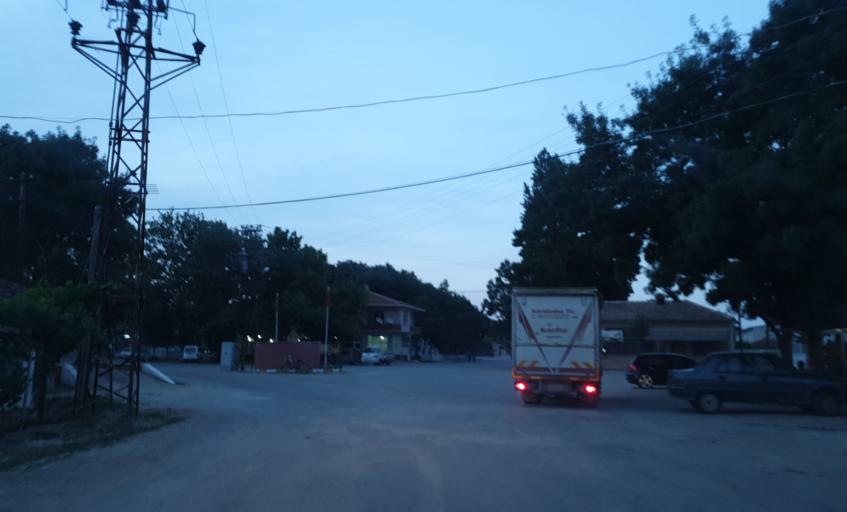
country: TR
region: Kirklareli
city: Vize
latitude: 41.4873
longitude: 27.7530
